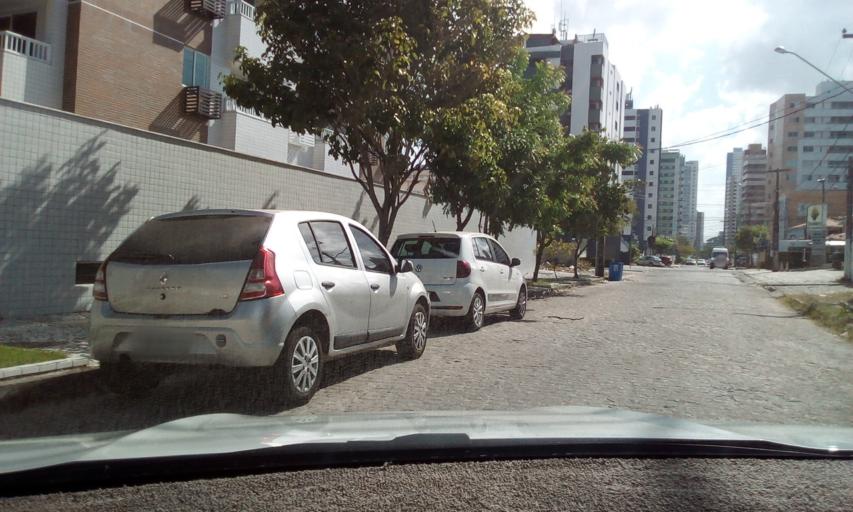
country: BR
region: Paraiba
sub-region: Joao Pessoa
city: Joao Pessoa
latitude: -7.0994
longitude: -34.8339
